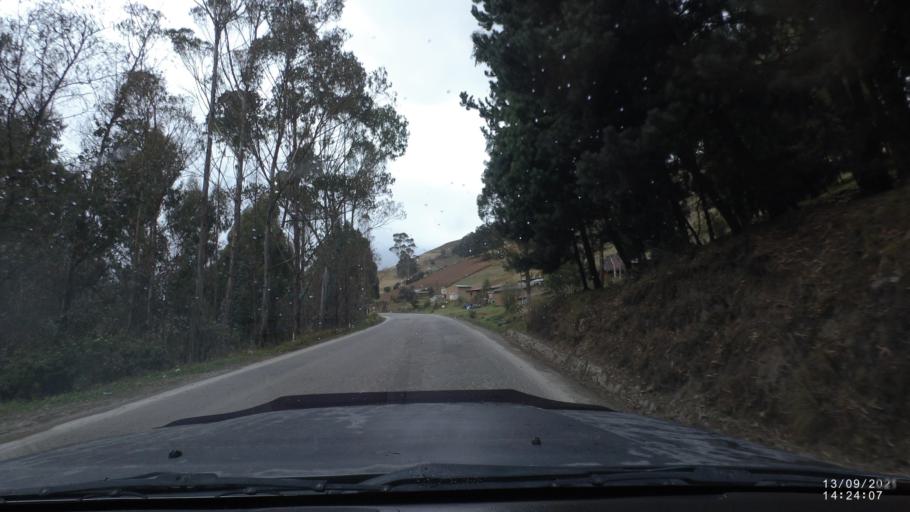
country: BO
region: Cochabamba
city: Colomi
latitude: -17.2819
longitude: -65.8739
